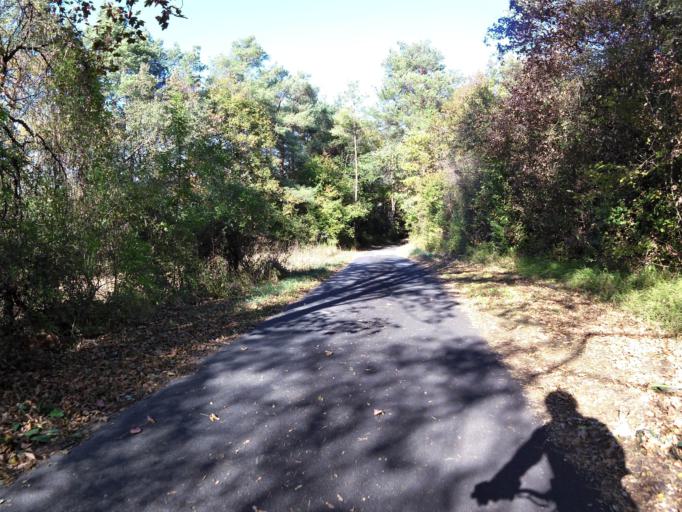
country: DE
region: Bavaria
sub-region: Regierungsbezirk Unterfranken
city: Reichenberg
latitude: 49.7455
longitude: 9.9367
